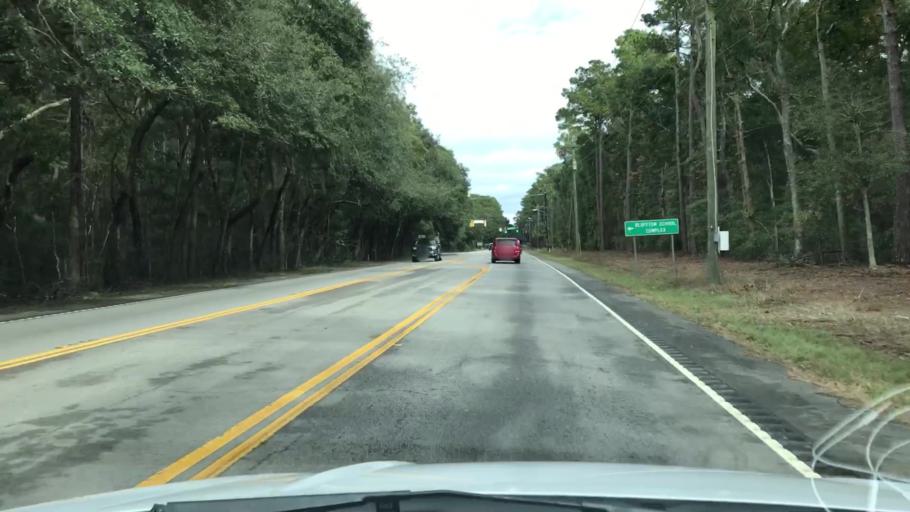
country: US
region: South Carolina
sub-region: Beaufort County
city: Bluffton
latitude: 32.2336
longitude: -80.9039
